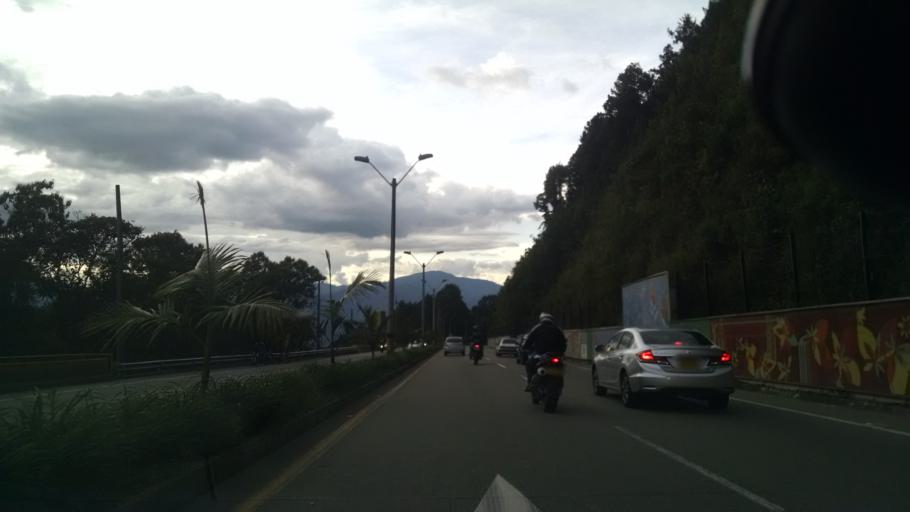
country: CO
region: Antioquia
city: Envigado
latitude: 6.1546
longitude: -75.5451
